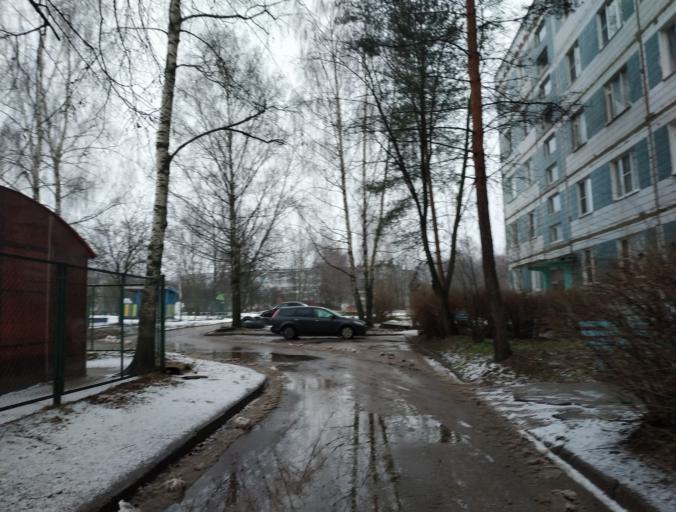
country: RU
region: Moskovskaya
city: Taldom
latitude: 56.7402
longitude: 37.5308
